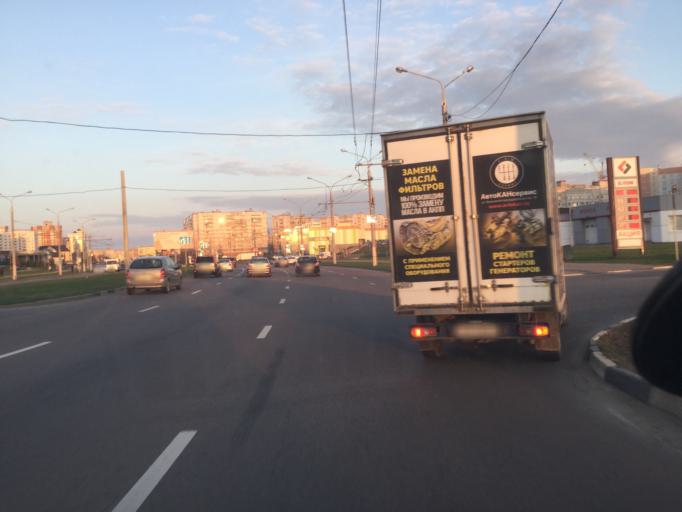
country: BY
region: Vitebsk
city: Vitebsk
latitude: 55.1644
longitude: 30.2035
